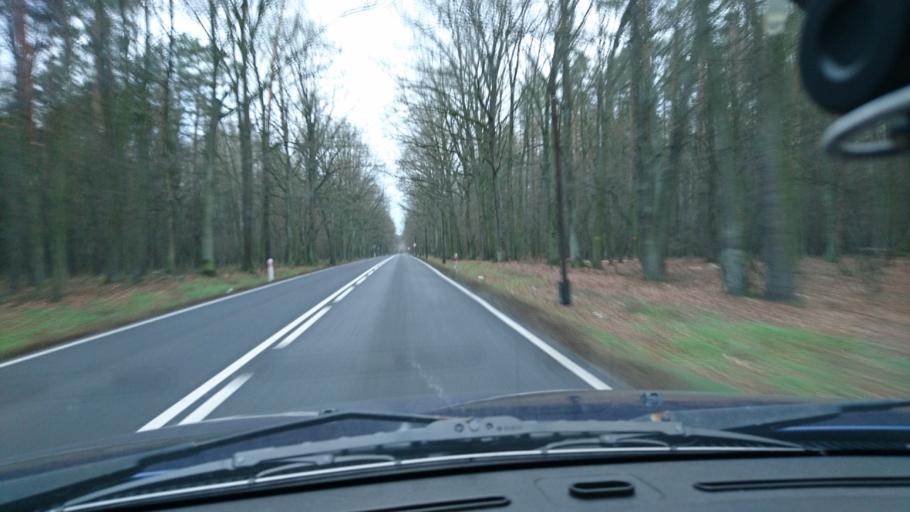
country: PL
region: Opole Voivodeship
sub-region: Powiat kluczborski
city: Kluczbork
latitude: 50.9484
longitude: 18.3148
